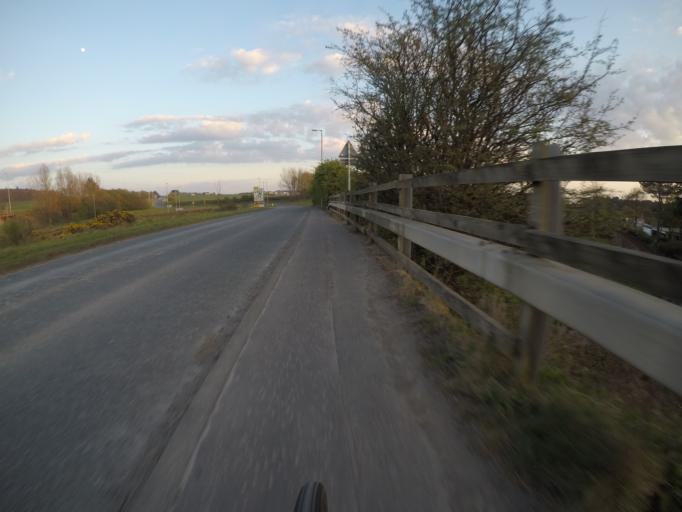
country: GB
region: Scotland
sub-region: South Ayrshire
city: Troon
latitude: 55.5687
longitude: -4.6393
